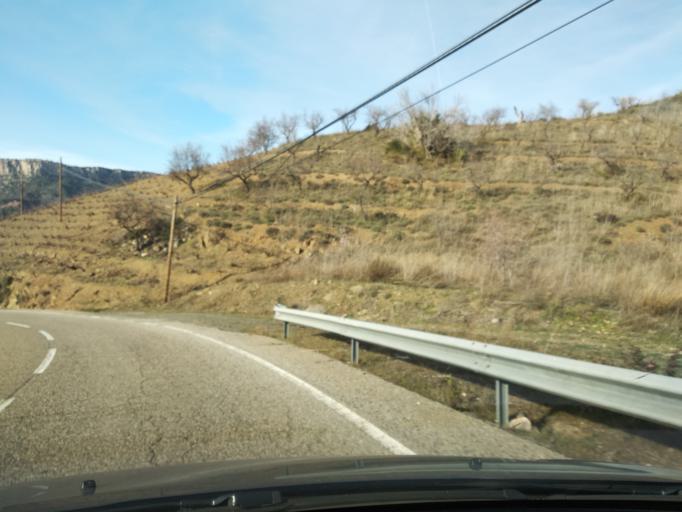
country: ES
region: Catalonia
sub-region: Provincia de Tarragona
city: Margalef
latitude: 41.2124
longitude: 0.7705
